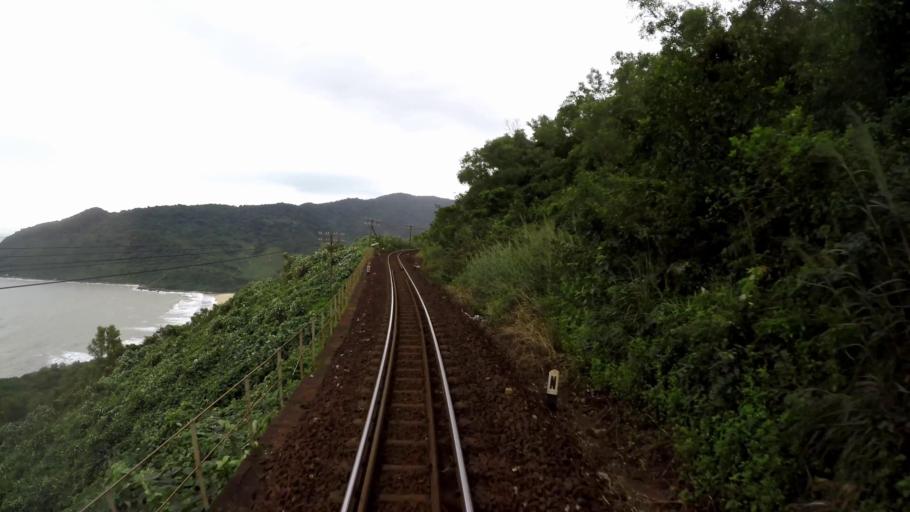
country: VN
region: Da Nang
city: Lien Chieu
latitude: 16.2135
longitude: 108.1343
